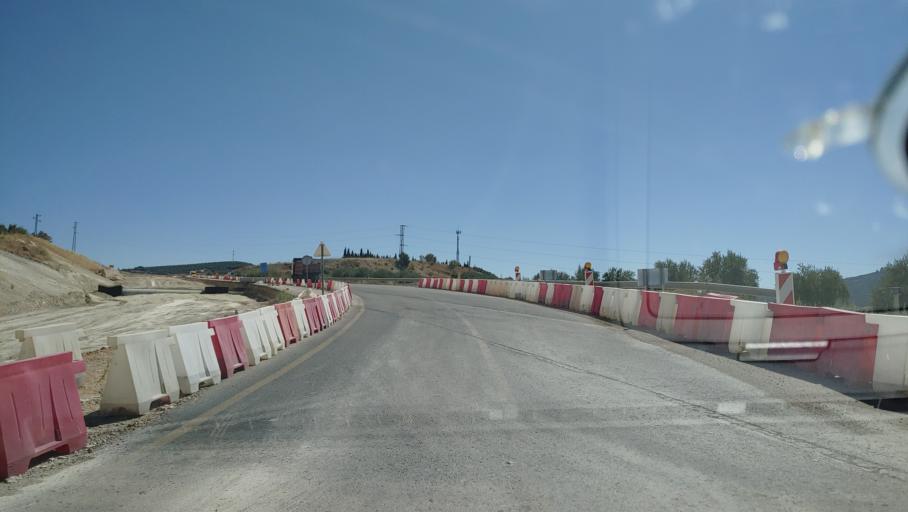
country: ES
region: Andalusia
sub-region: Provincia de Jaen
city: Villanueva del Arzobispo
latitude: 38.1719
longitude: -2.9915
